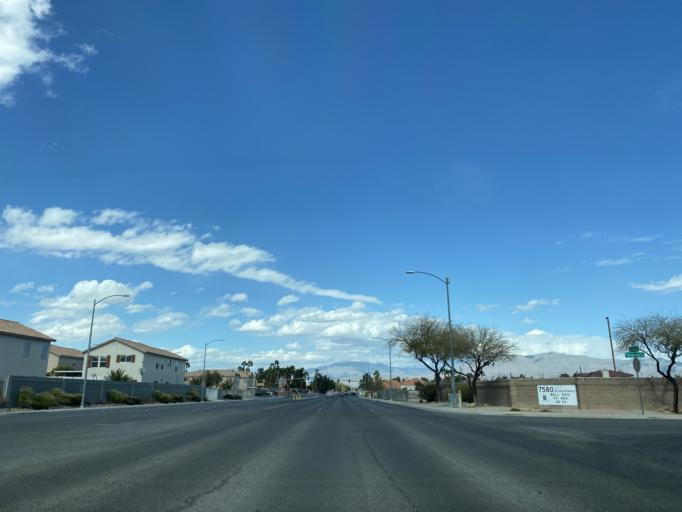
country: US
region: Nevada
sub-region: Clark County
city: Spring Valley
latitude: 36.2309
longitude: -115.2606
